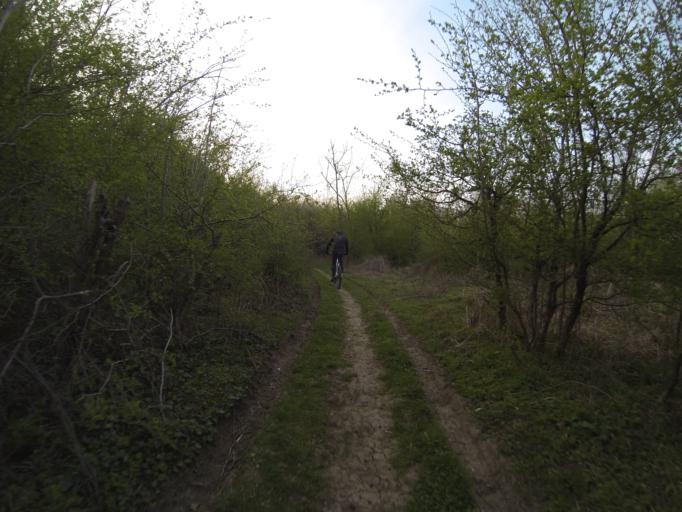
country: RO
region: Dolj
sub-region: Comuna Bucovat
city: Bucovat
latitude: 44.2869
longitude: 23.7527
